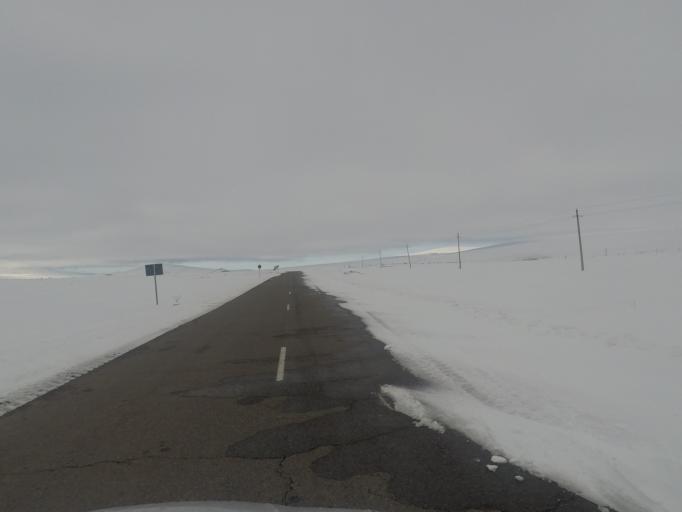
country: GE
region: Samtskhe-Javakheti
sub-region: Ninotsminda
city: Ninotsminda
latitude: 41.4028
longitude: 43.8047
